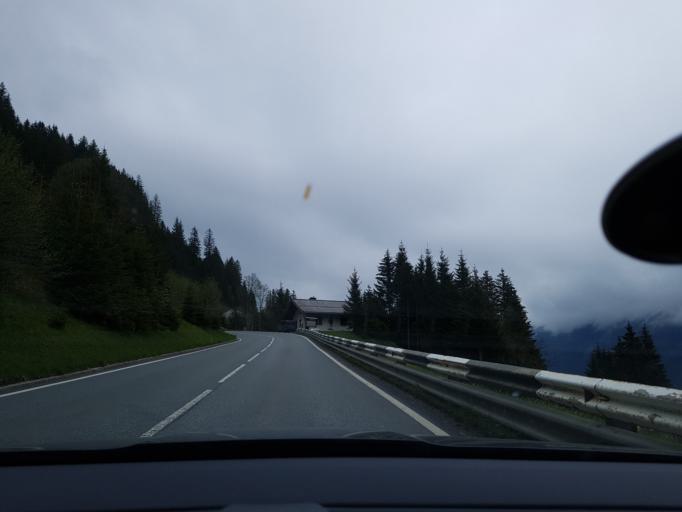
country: AT
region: Salzburg
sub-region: Politischer Bezirk Zell am See
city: Krimml
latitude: 47.2219
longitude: 12.1517
